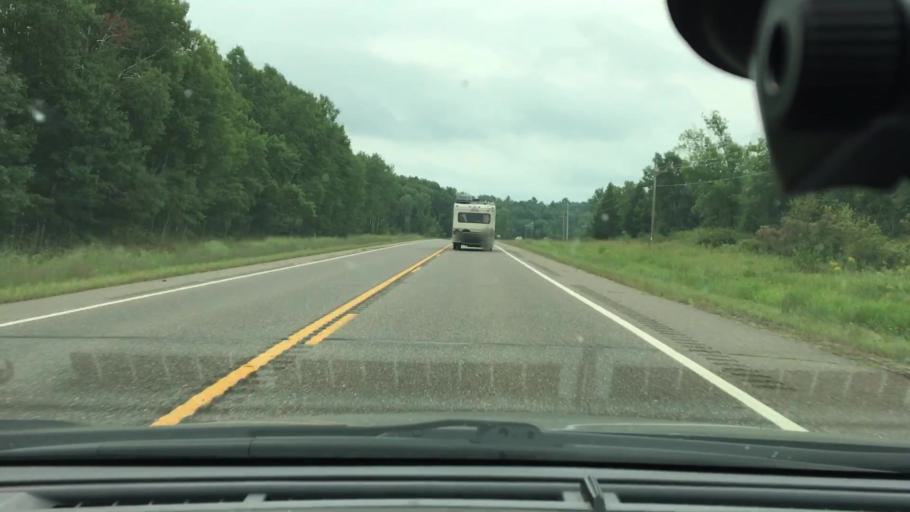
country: US
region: Minnesota
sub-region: Crow Wing County
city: Crosby
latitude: 46.5066
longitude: -93.9591
